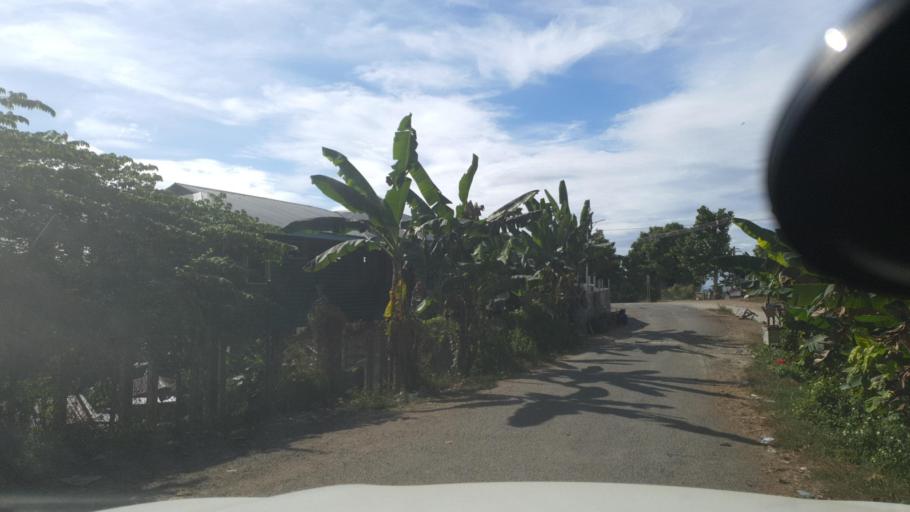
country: SB
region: Guadalcanal
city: Honiara
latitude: -9.4380
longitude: 159.9461
